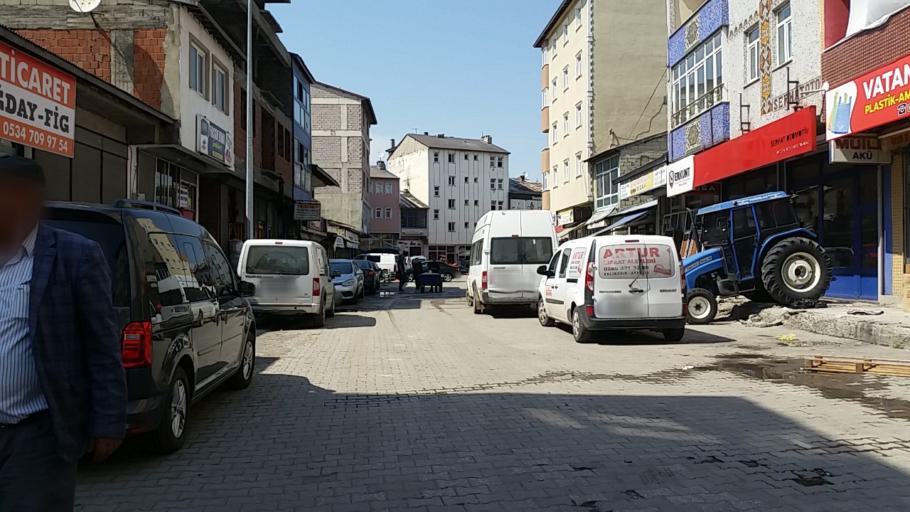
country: TR
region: Agri
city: Agri
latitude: 39.7147
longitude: 43.0521
